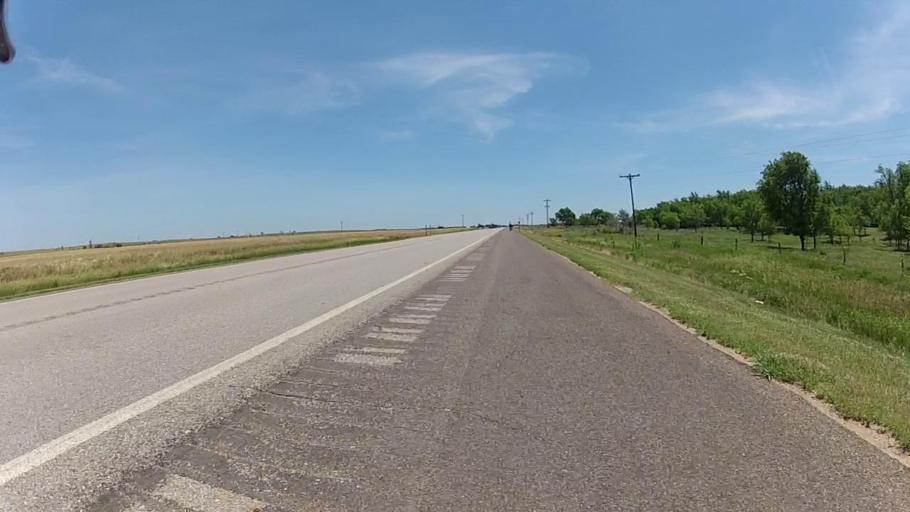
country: US
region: Kansas
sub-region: Barber County
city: Medicine Lodge
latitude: 37.2536
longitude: -98.3703
